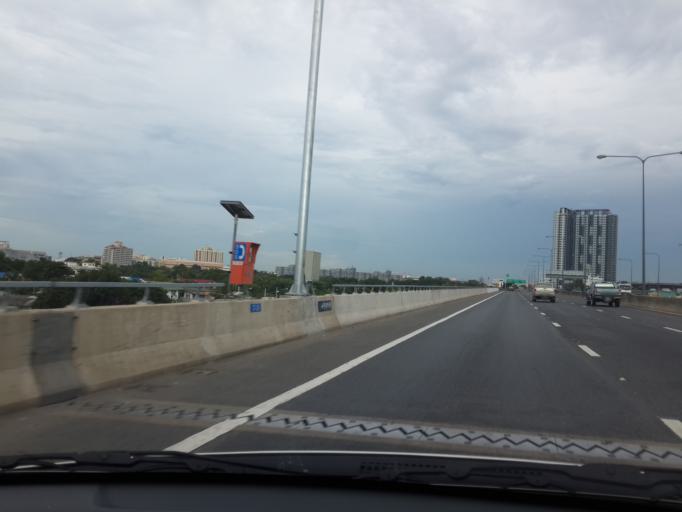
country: TH
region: Bangkok
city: Watthana
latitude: 13.7526
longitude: 100.5993
